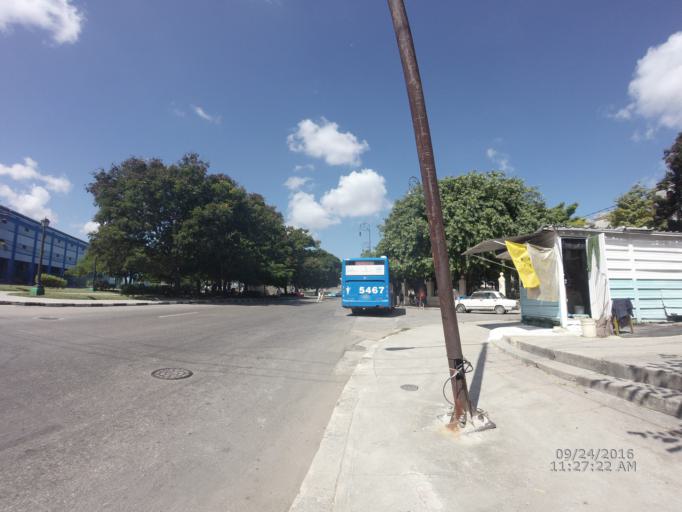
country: CU
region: La Habana
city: La Habana Vieja
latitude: 23.1287
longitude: -82.3516
